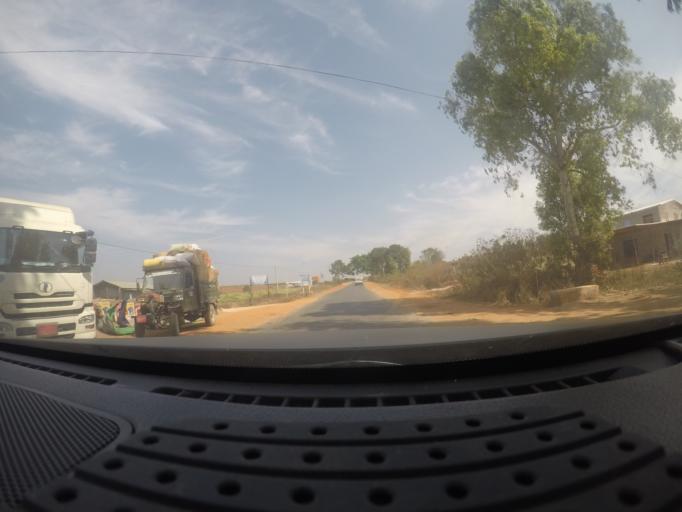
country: MM
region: Shan
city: Taunggyi
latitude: 20.7041
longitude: 96.6277
